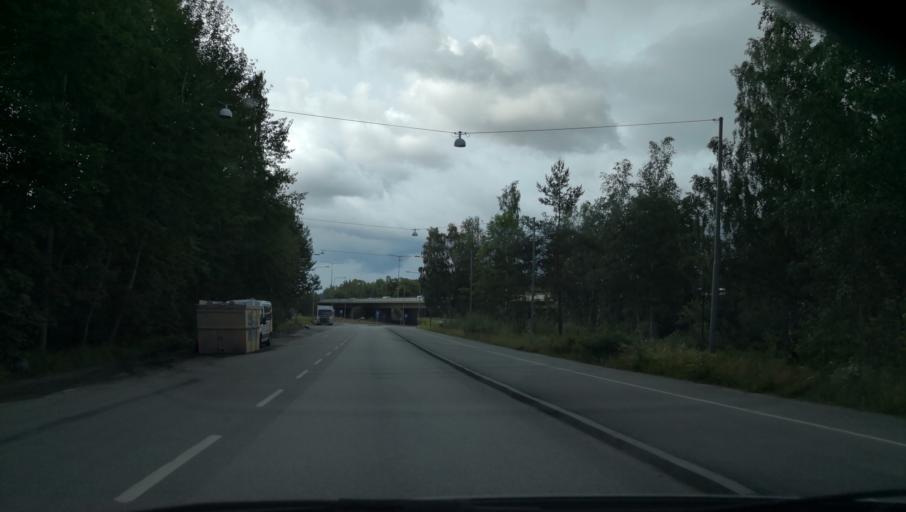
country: SE
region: Stockholm
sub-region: Nacka Kommun
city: Alta
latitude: 59.2397
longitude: 18.1195
